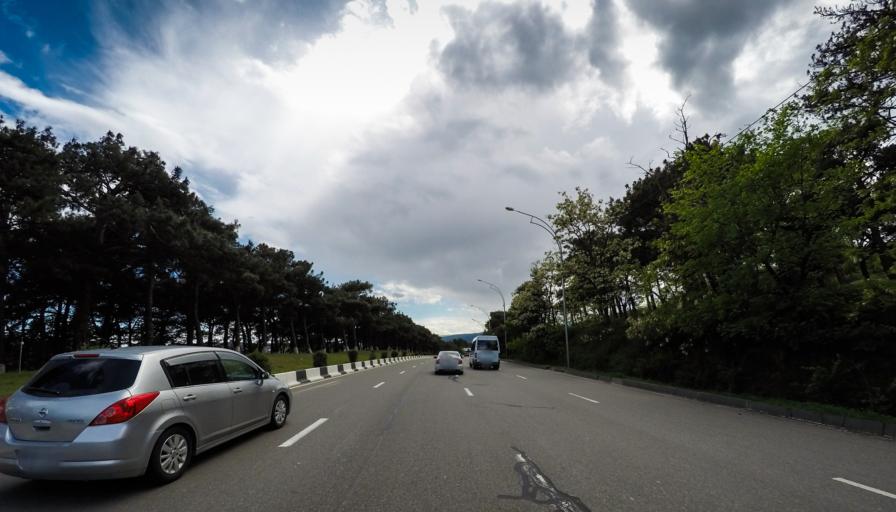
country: GE
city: Zahesi
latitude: 41.8140
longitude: 44.7716
